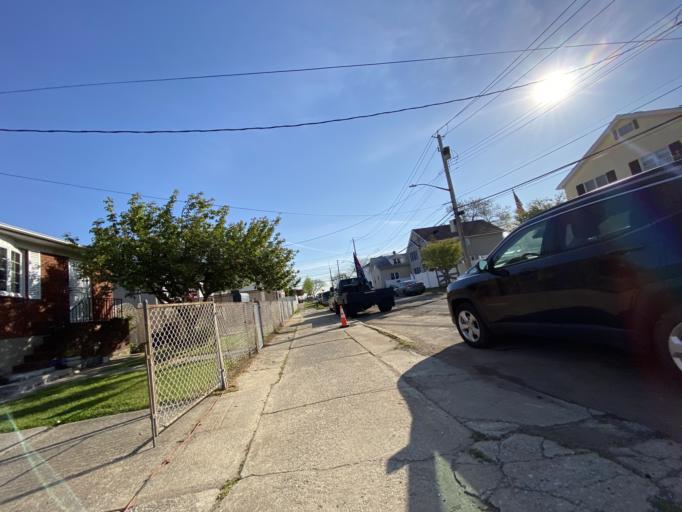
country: US
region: New York
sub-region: Richmond County
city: Staten Island
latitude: 40.5649
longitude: -74.1008
